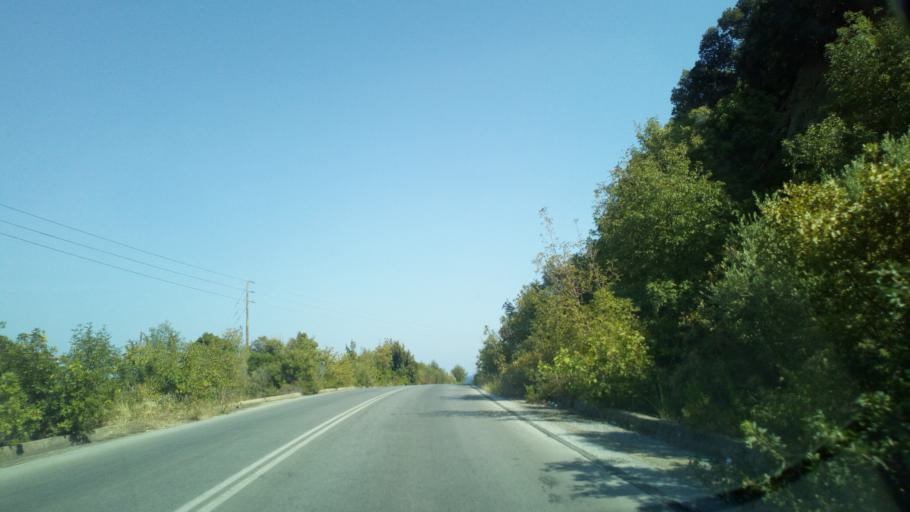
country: GR
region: Central Macedonia
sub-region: Nomos Thessalonikis
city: Stavros
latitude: 40.6329
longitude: 23.7597
